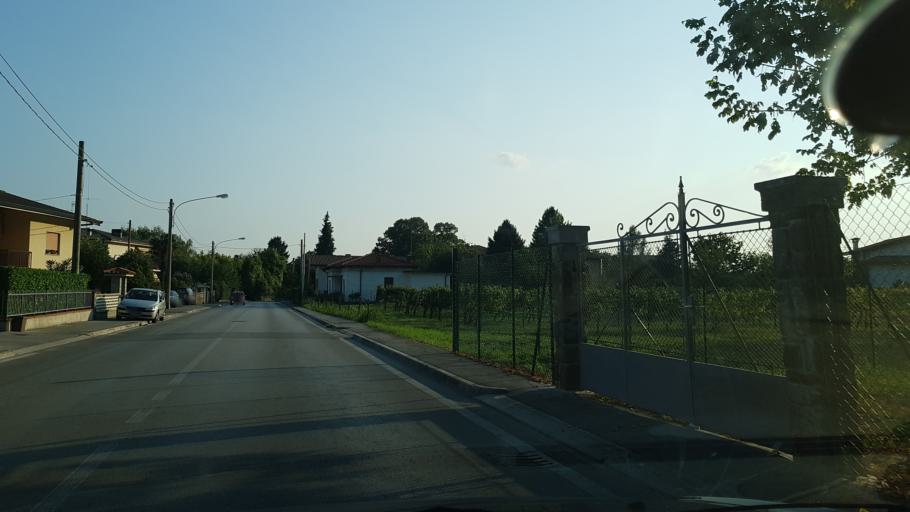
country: IT
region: Friuli Venezia Giulia
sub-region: Provincia di Gorizia
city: Gorizia
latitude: 45.9442
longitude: 13.5992
